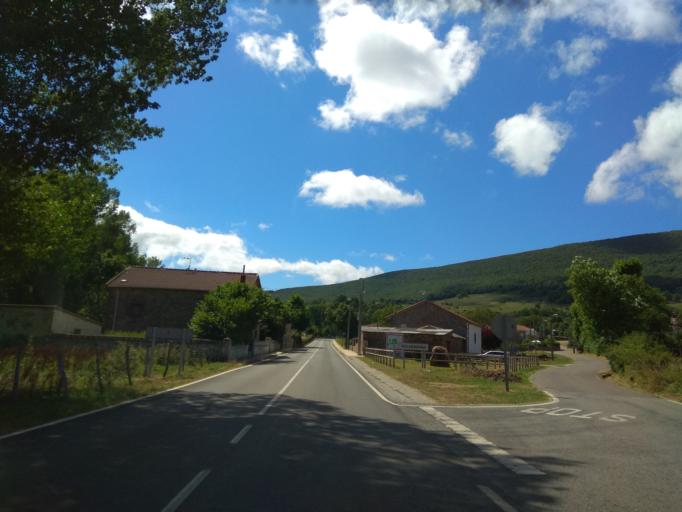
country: ES
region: Cantabria
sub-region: Provincia de Cantabria
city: Villaescusa
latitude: 42.9657
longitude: -4.1660
